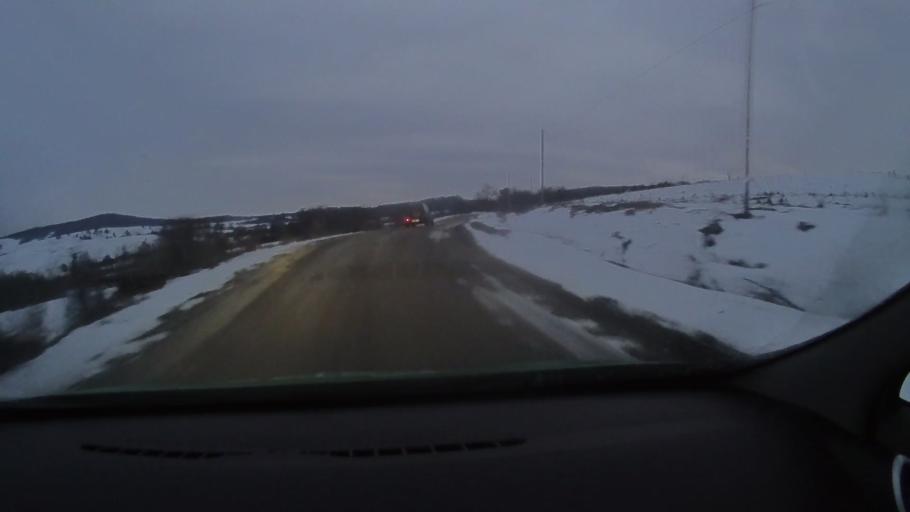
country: RO
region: Harghita
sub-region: Comuna Darjiu
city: Darjiu
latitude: 46.1914
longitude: 25.2466
